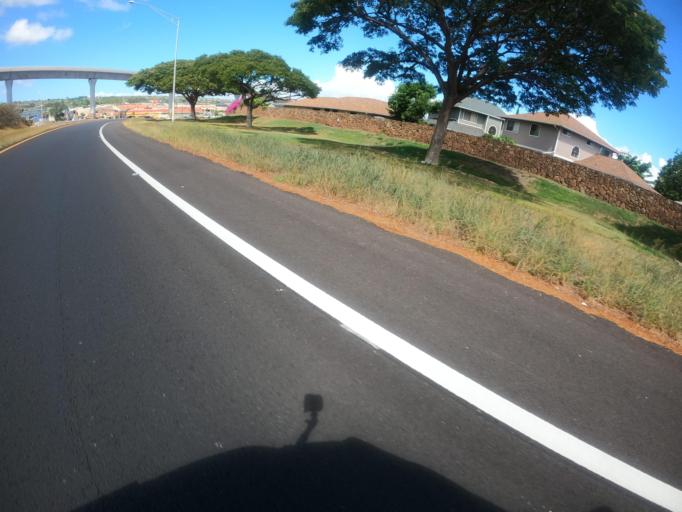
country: US
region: Hawaii
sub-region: Honolulu County
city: Royal Kunia
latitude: 21.3753
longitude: -158.0260
